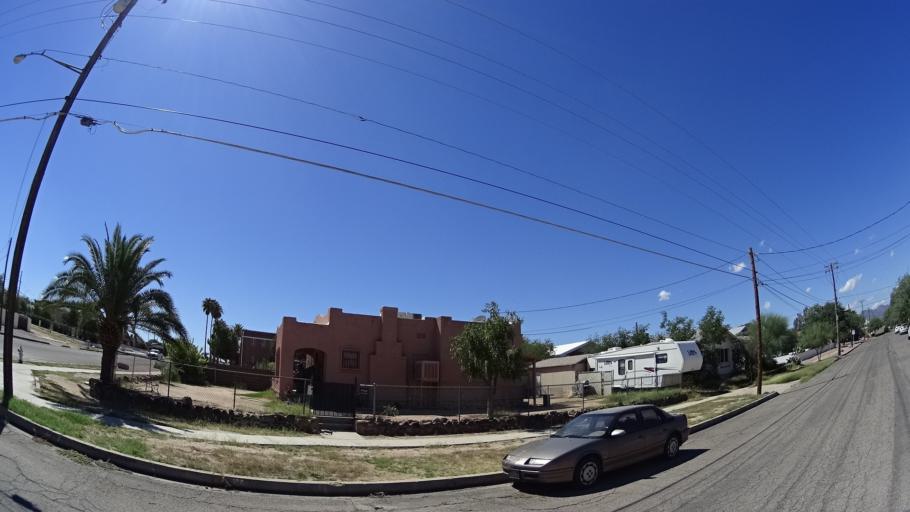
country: US
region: Arizona
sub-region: Pima County
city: South Tucson
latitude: 32.2373
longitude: -110.9643
